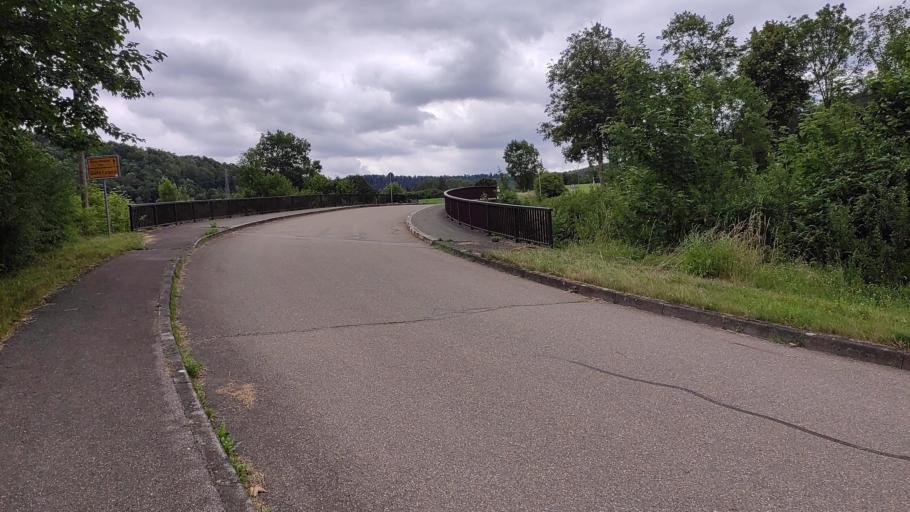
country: DE
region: Baden-Wuerttemberg
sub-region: Tuebingen Region
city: Stetten am Kalten Markt
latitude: 48.0796
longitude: 9.1086
